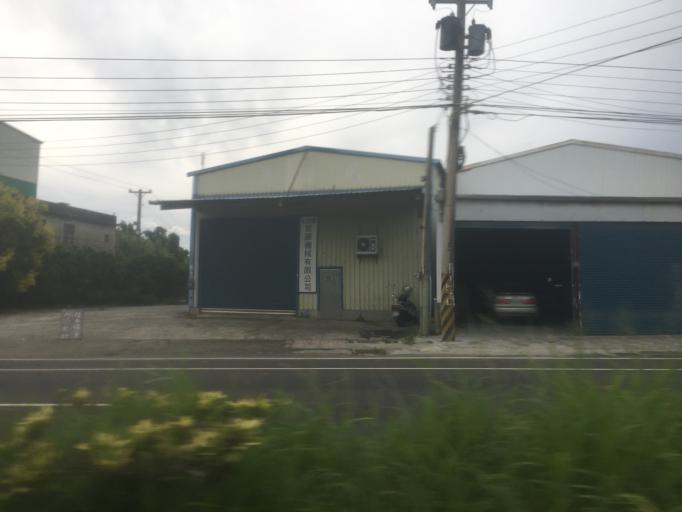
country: TW
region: Taiwan
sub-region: Hsinchu
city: Zhubei
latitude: 24.8844
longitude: 121.0382
